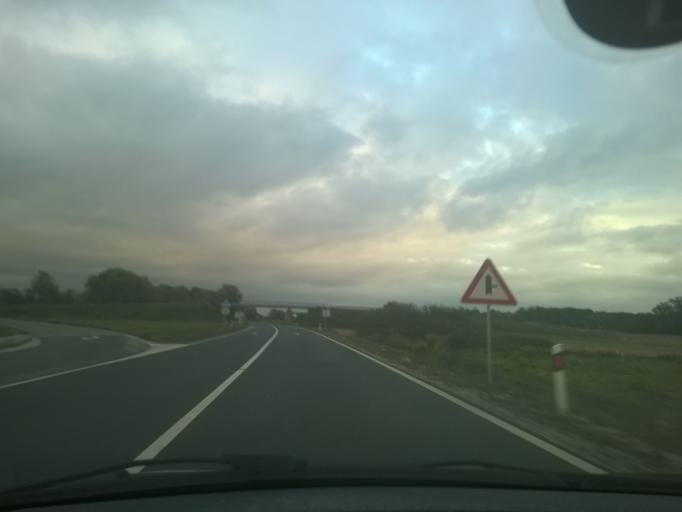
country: HR
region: Zagrebacka
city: Pojatno
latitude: 45.9099
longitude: 15.8156
